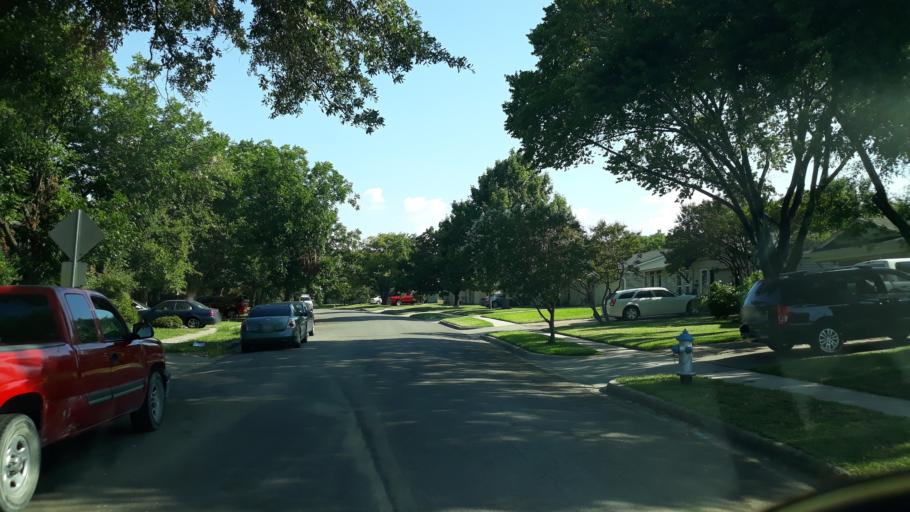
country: US
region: Texas
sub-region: Dallas County
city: Irving
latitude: 32.8491
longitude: -97.0065
